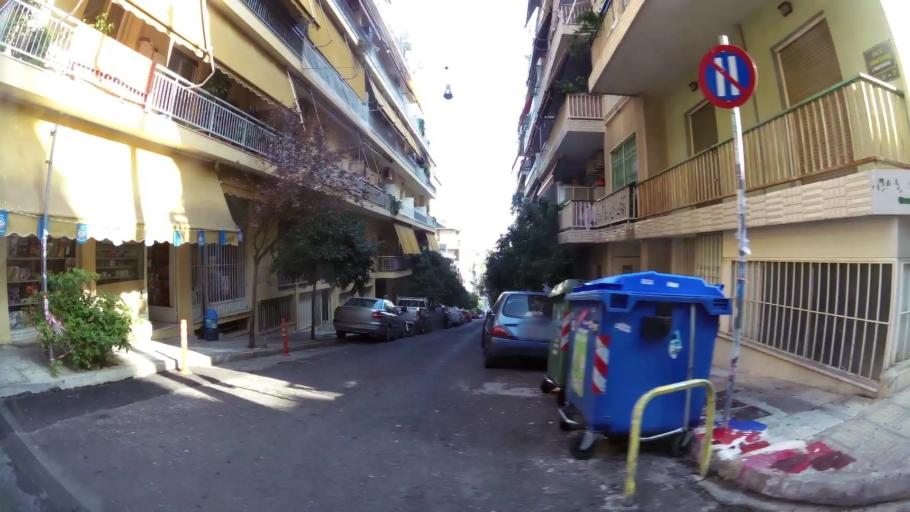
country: GR
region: Attica
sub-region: Nomarchia Athinas
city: Kaisariani
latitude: 37.9755
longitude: 23.7703
